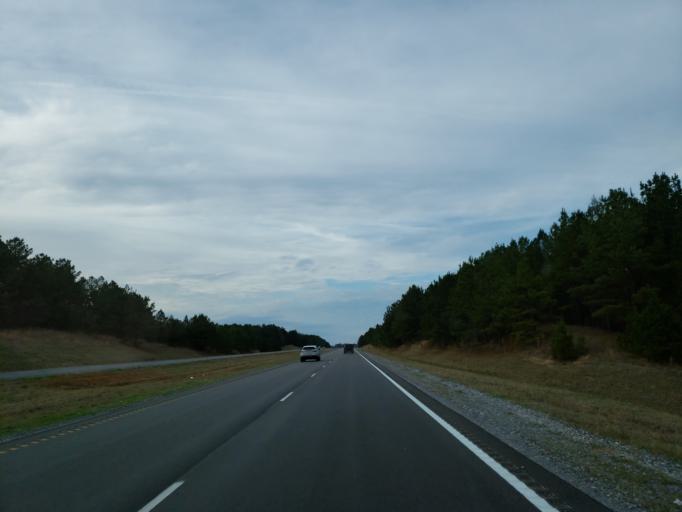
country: US
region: Mississippi
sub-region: Clarke County
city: Quitman
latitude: 32.0833
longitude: -88.6939
